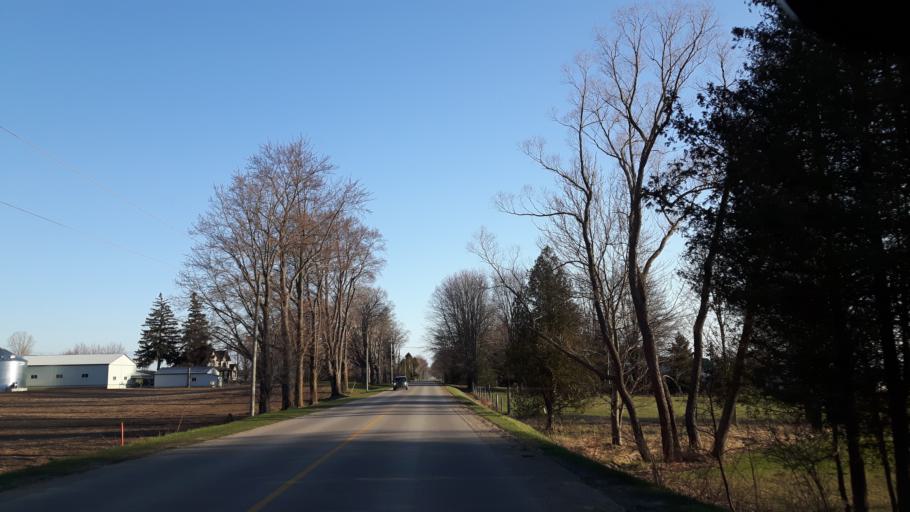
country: CA
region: Ontario
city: Goderich
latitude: 43.7130
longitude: -81.6852
